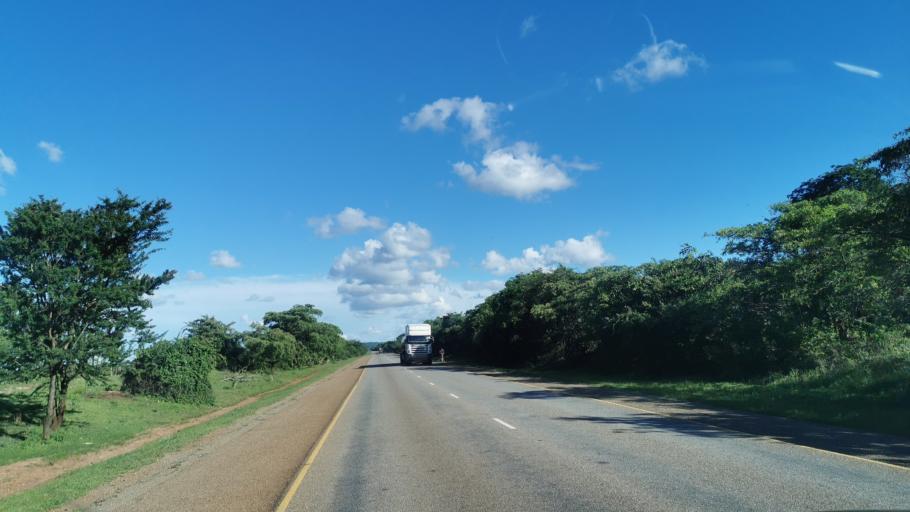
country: TZ
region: Geita
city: Masumbwe
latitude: -3.7196
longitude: 32.2959
